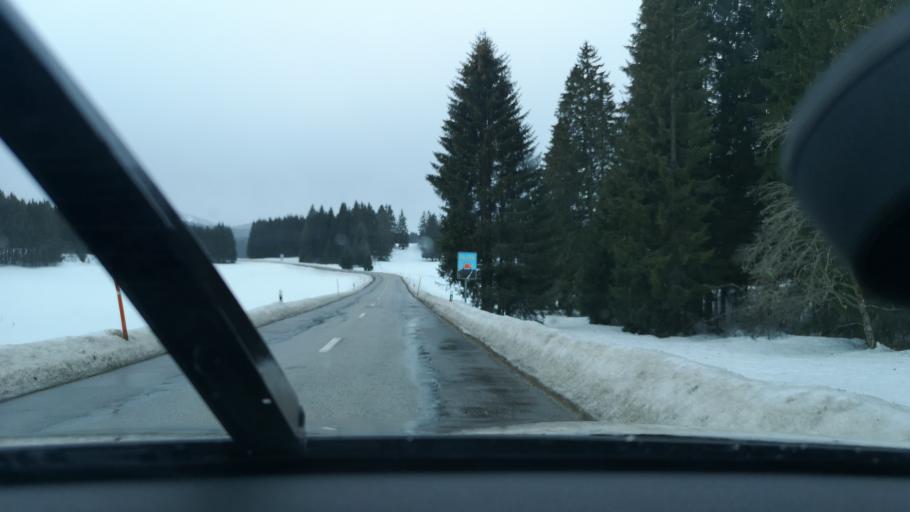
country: FR
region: Franche-Comte
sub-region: Departement du Doubs
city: Les Fourgs
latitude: 46.8229
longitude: 6.4402
